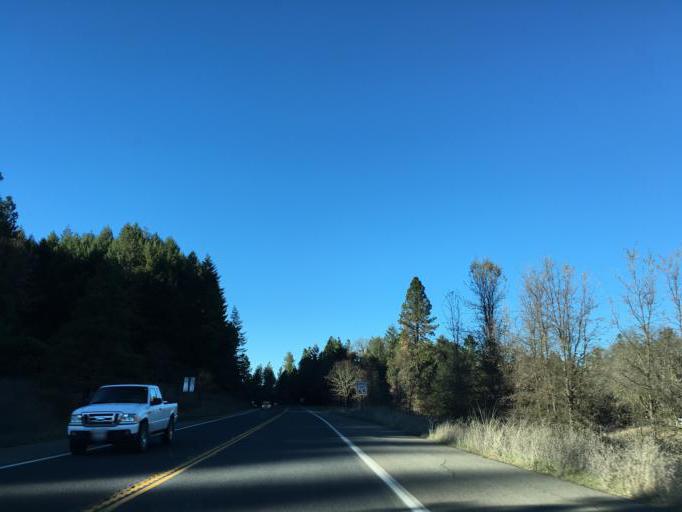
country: US
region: California
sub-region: Mendocino County
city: Laytonville
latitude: 39.7092
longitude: -123.4905
